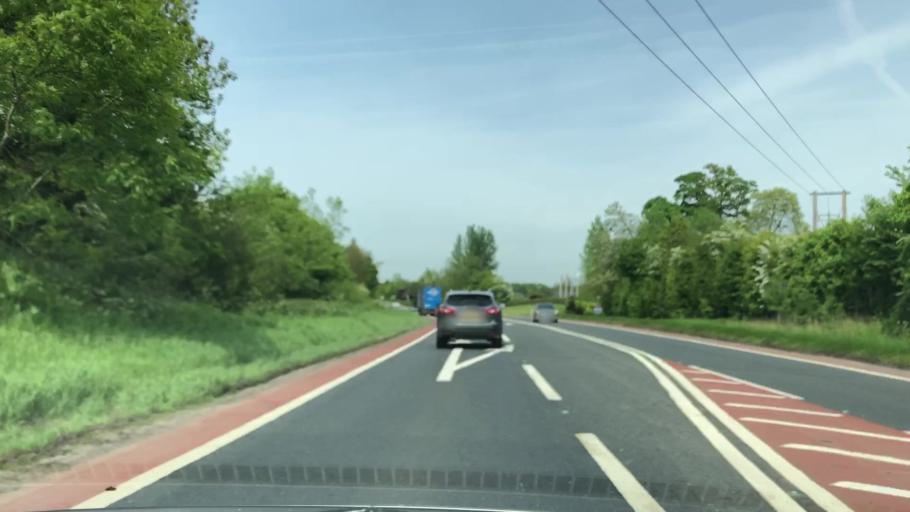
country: GB
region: England
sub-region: Shropshire
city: Gobowen
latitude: 52.9105
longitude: -3.0422
